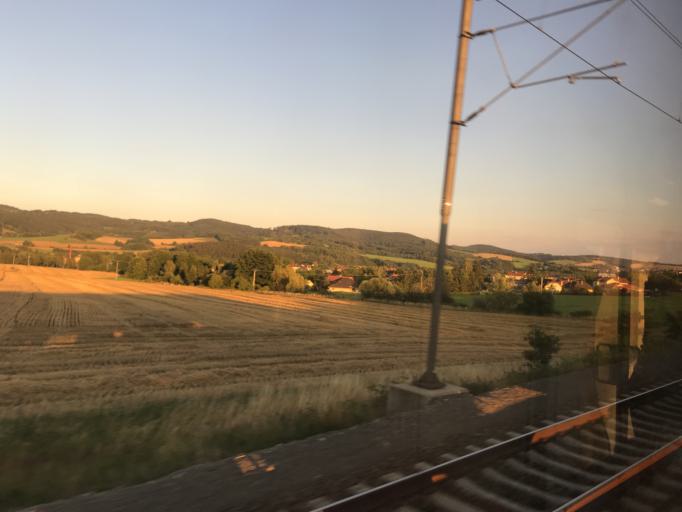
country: CZ
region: Central Bohemia
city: Votice
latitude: 49.6762
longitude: 14.6270
